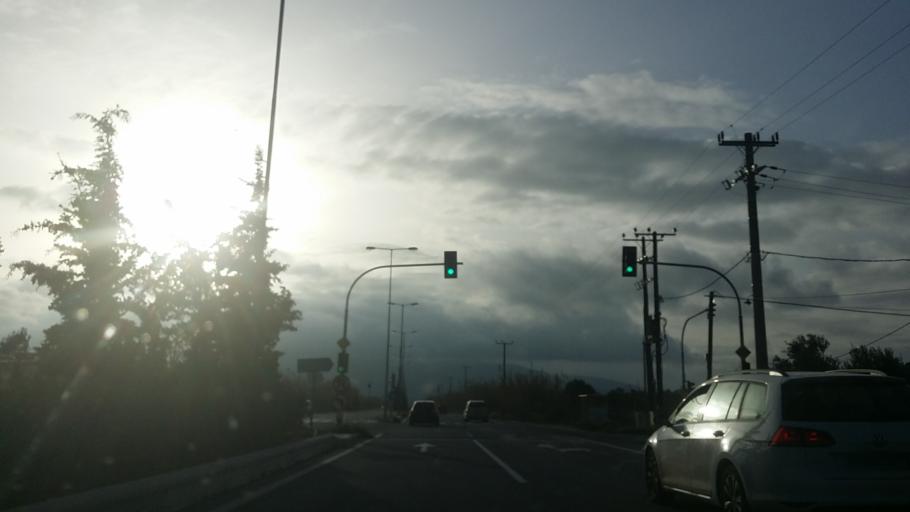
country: GR
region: Attica
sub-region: Nomarchia Anatolikis Attikis
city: Keratea
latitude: 37.8033
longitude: 24.0361
